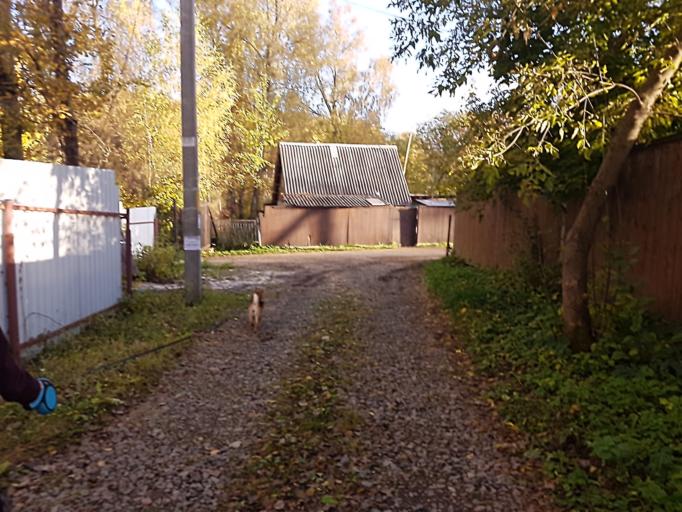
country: RU
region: Moskovskaya
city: Istra
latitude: 55.9192
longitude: 36.8861
